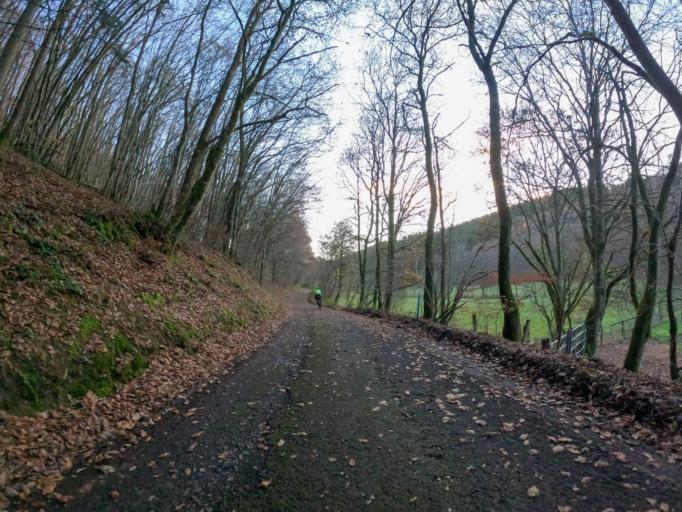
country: LU
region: Diekirch
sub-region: Canton de Wiltz
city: Bavigne
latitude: 49.9299
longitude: 5.8447
